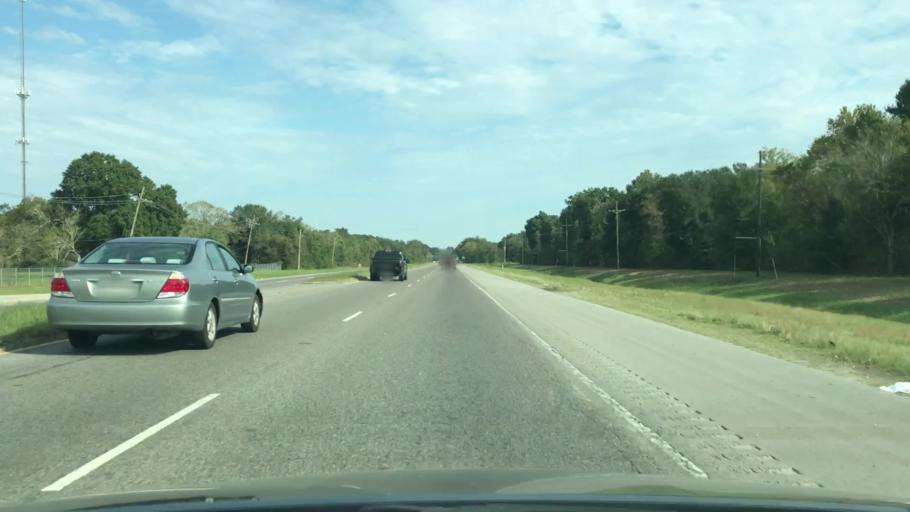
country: US
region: Louisiana
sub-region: Jefferson Parish
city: Avondale
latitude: 29.9097
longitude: -90.1996
